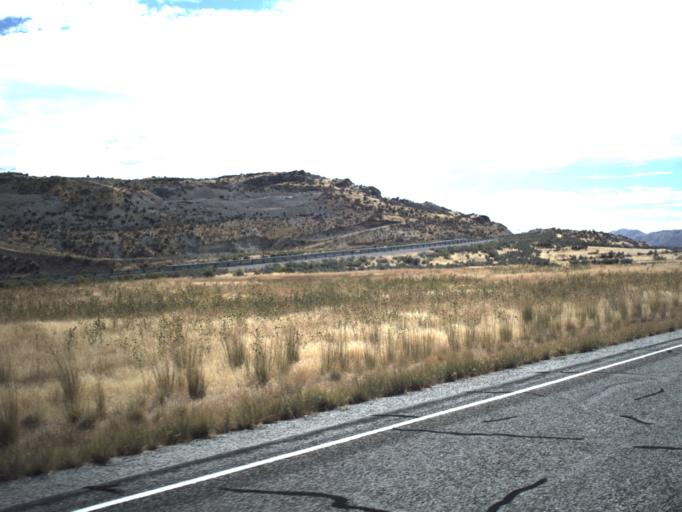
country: US
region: Utah
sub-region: Box Elder County
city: Tremonton
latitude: 41.6749
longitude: -112.4458
